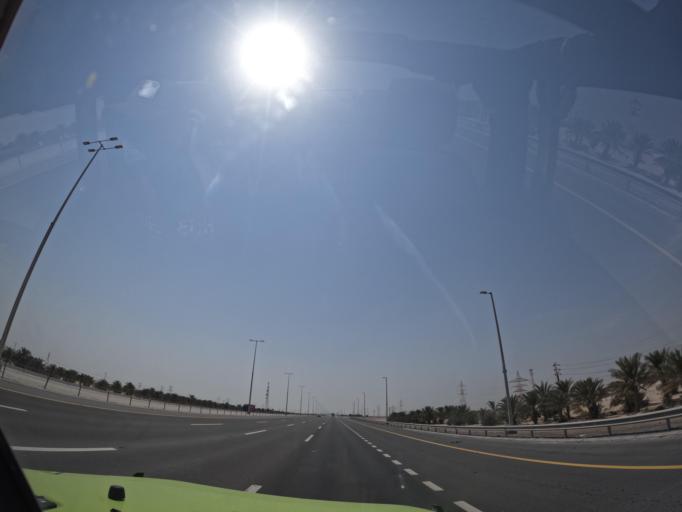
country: AE
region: Abu Dhabi
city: Abu Dhabi
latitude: 24.1796
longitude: 54.3732
